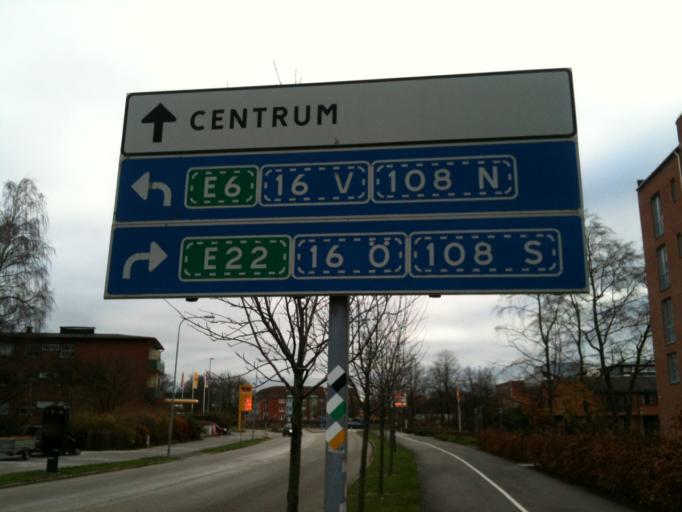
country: SE
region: Skane
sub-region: Lunds Kommun
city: Lund
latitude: 55.7028
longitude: 13.1747
